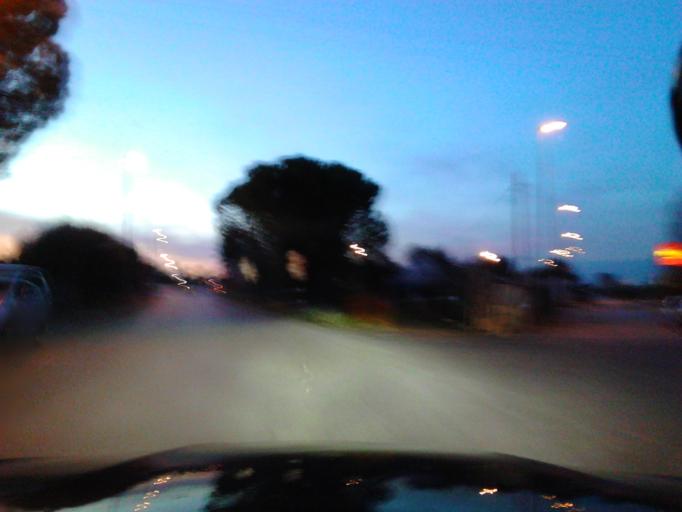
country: IT
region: Apulia
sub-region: Provincia di Bari
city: Adelfia
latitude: 41.0053
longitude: 16.8606
